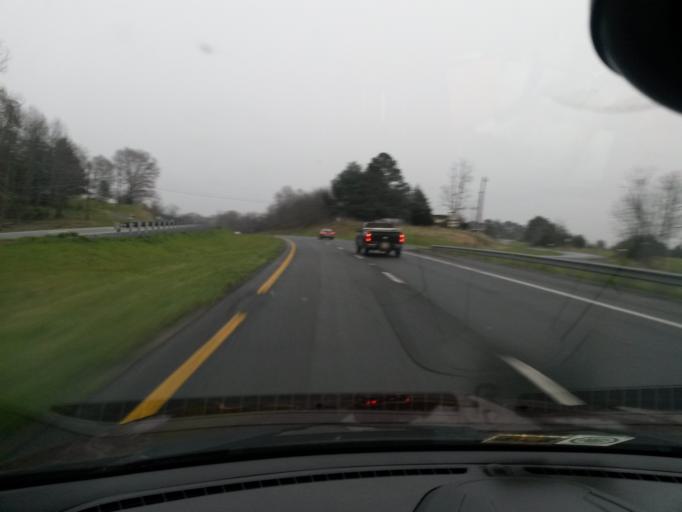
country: US
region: Virginia
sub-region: City of Bedford
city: Bedford
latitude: 37.3131
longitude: -79.4747
